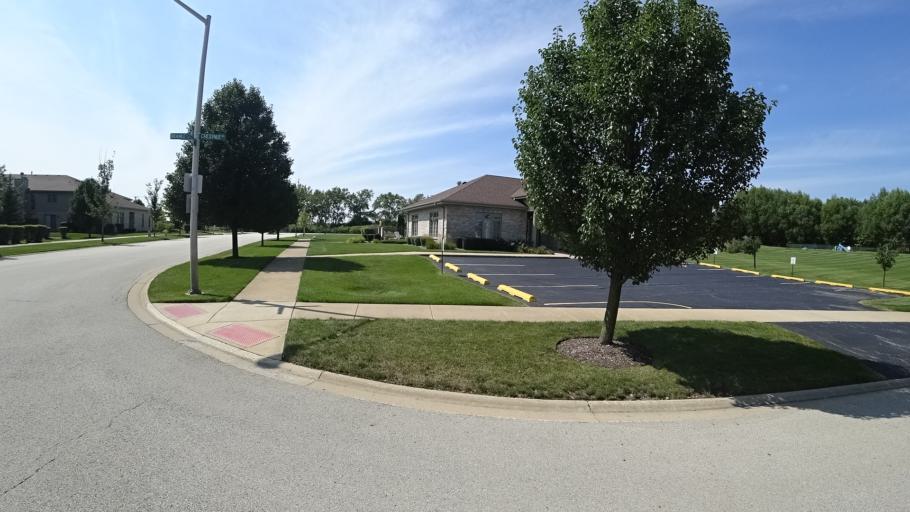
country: US
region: Illinois
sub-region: Cook County
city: Orland Hills
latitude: 41.5616
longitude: -87.8450
